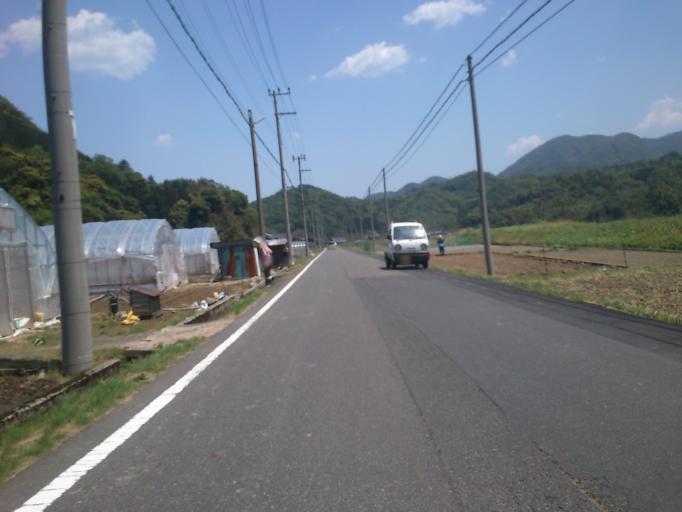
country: JP
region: Kyoto
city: Miyazu
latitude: 35.7392
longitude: 135.1579
